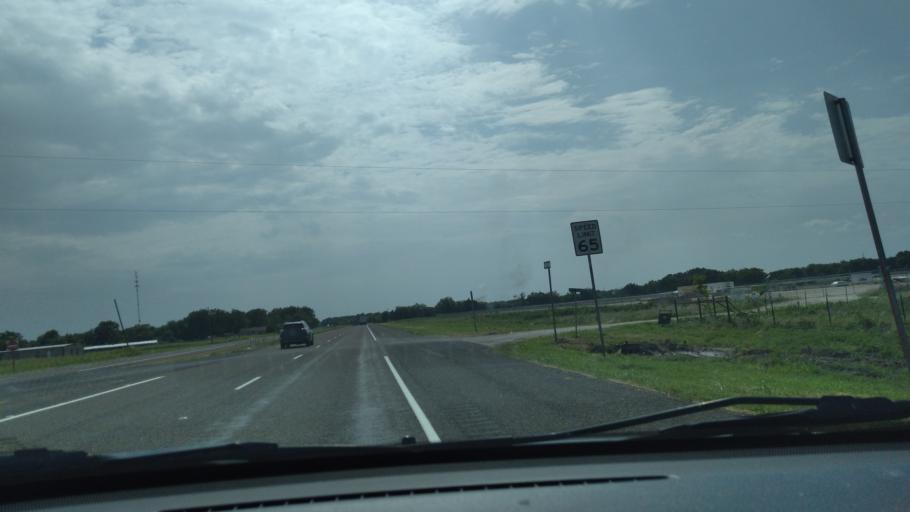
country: US
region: Texas
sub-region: Navarro County
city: Kerens
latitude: 32.1299
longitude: -96.2529
